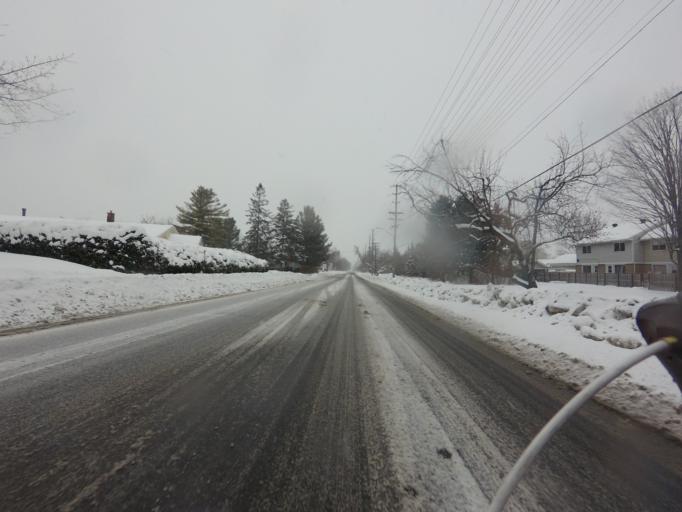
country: CA
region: Ontario
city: Ottawa
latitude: 45.3577
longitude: -75.6451
